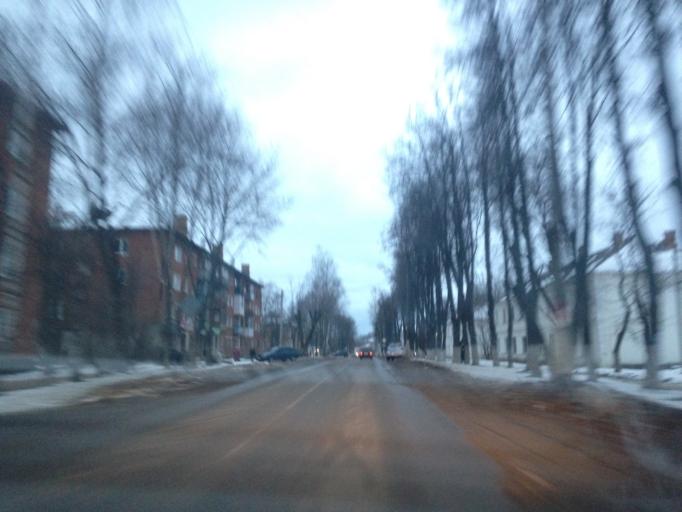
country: RU
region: Tula
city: Shchekino
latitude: 53.9984
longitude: 37.5230
